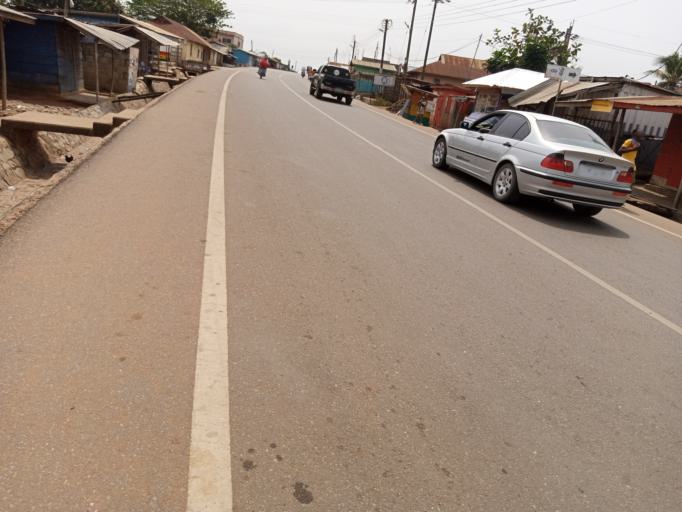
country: GH
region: Volta
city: Kpandu
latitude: 7.0042
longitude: 0.2956
